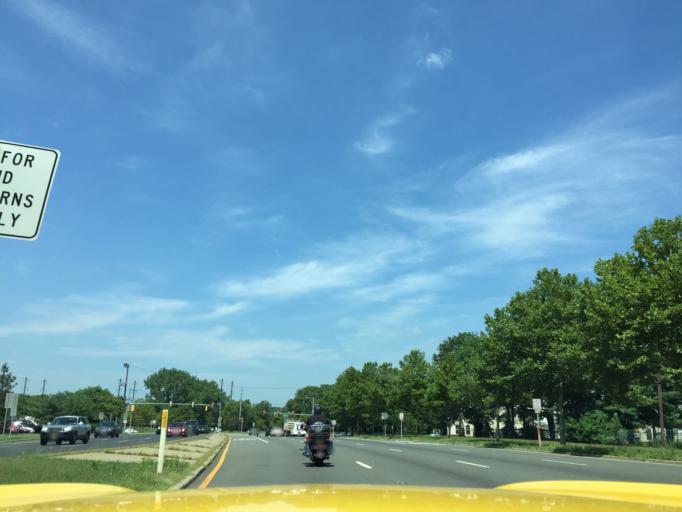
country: US
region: New Jersey
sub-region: Mercer County
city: Trenton
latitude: 40.2071
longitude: -74.7627
